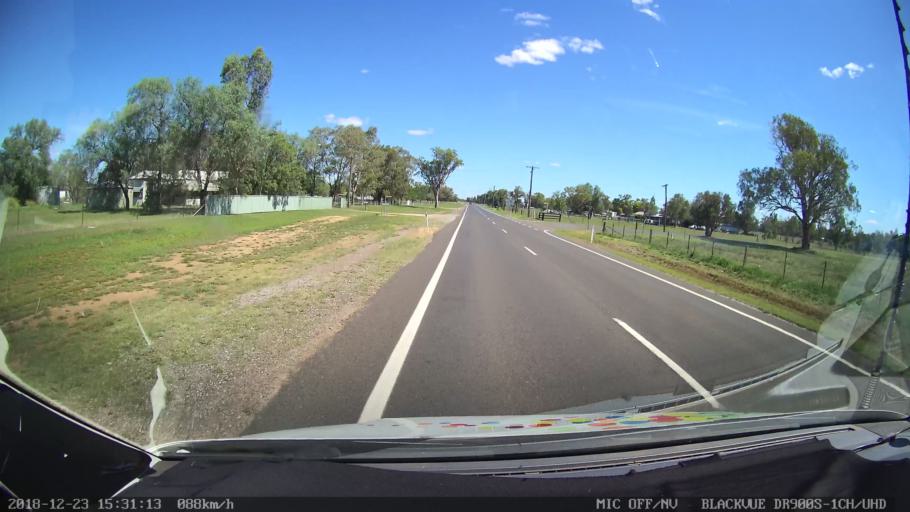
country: AU
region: New South Wales
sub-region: Tamworth Municipality
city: East Tamworth
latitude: -30.9690
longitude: 150.8666
